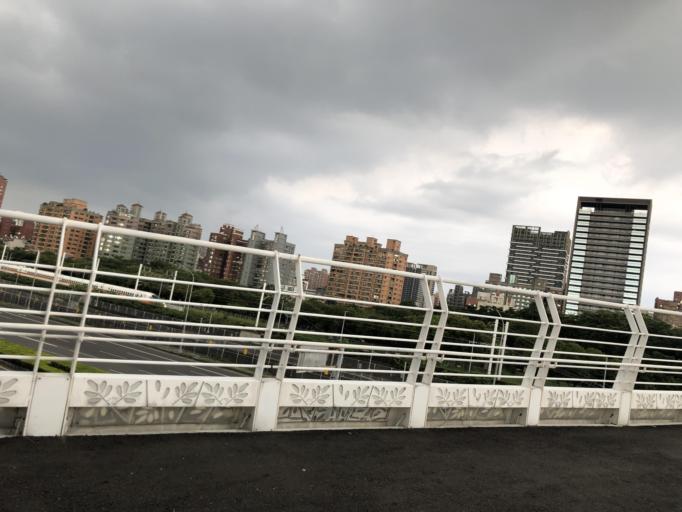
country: TW
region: Kaohsiung
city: Kaohsiung
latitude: 22.6800
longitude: 120.2986
